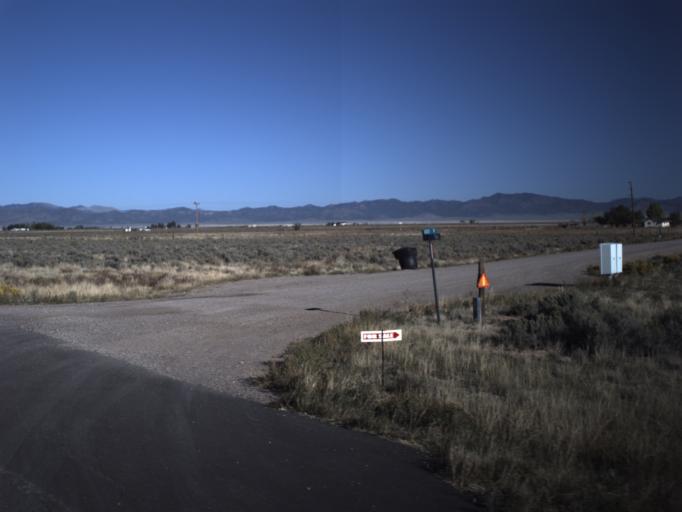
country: US
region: Utah
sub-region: Washington County
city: Enterprise
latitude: 37.7423
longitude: -113.7476
